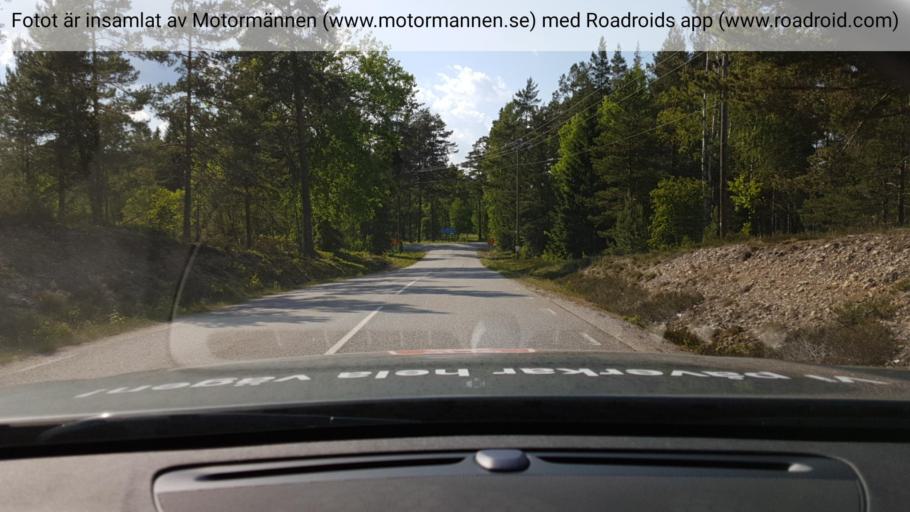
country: SE
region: Stockholm
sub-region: Varmdo Kommun
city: Mortnas
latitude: 59.2570
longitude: 18.4372
